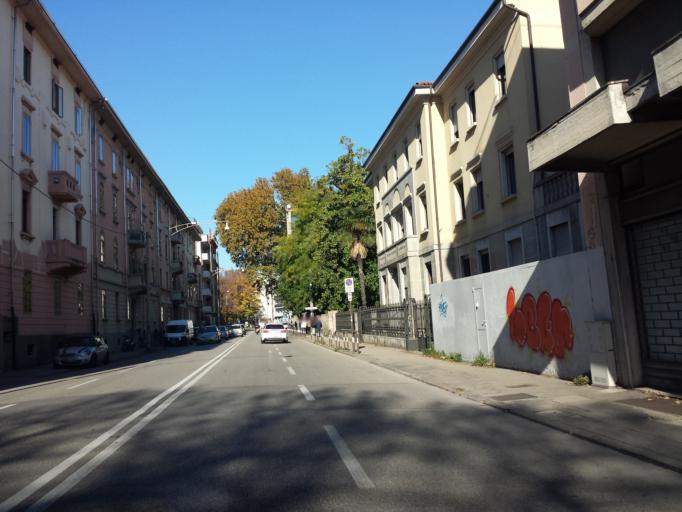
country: IT
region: Veneto
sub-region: Provincia di Padova
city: Padova
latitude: 45.4059
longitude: 11.8864
